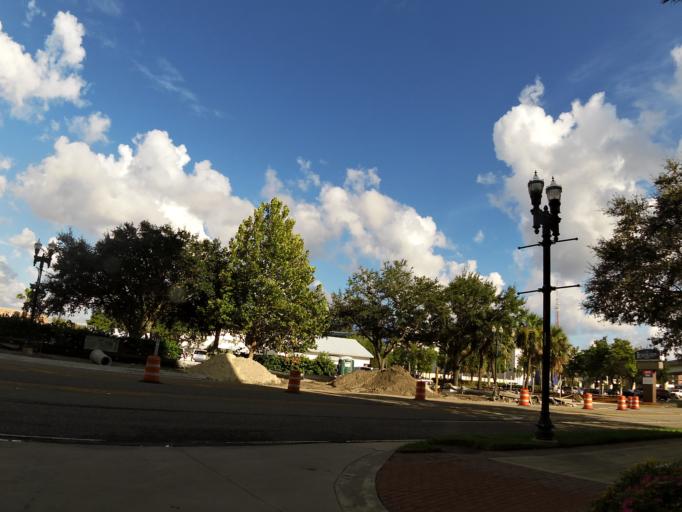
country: US
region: Florida
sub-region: Duval County
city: Jacksonville
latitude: 30.3168
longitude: -81.6537
